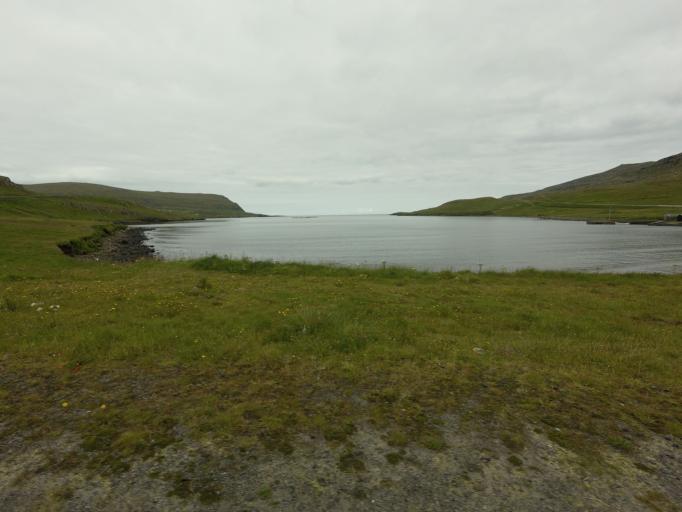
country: FO
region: Suduroy
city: Tvoroyri
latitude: 61.5349
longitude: -6.8121
